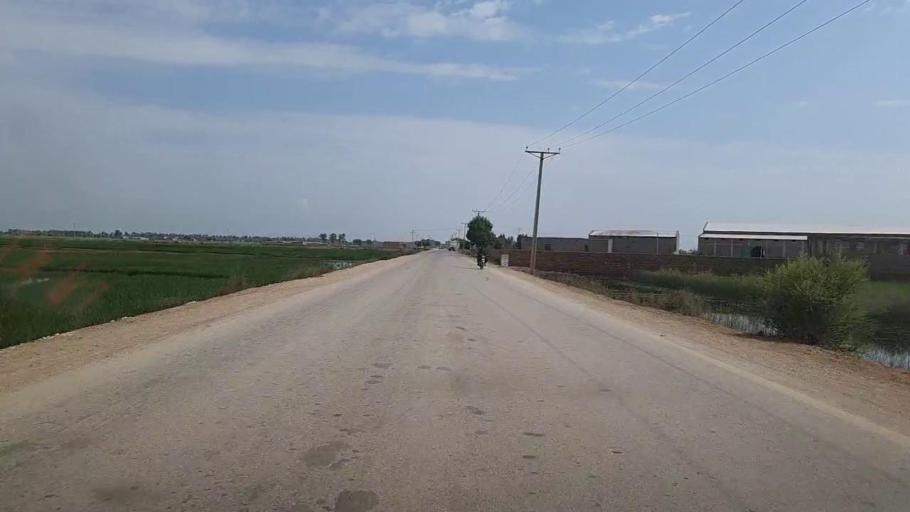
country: PK
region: Sindh
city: Thul
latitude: 28.2543
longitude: 68.7800
